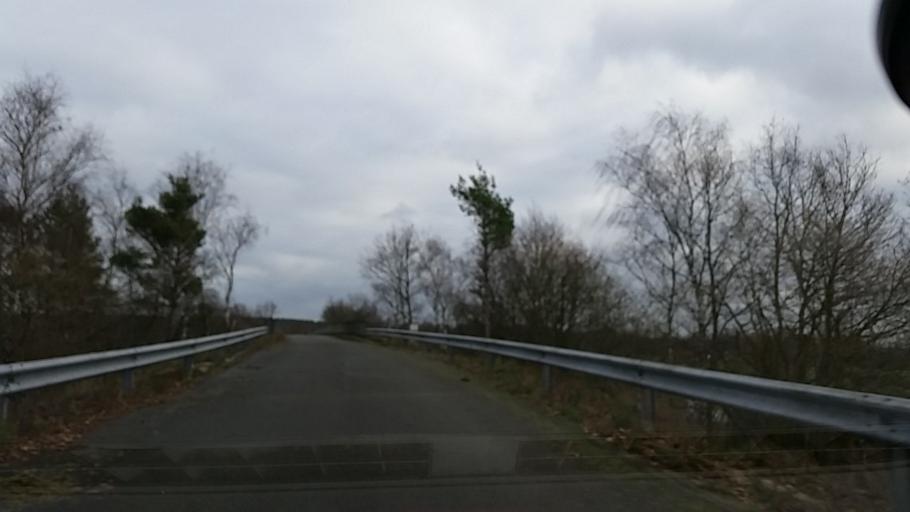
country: DE
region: Lower Saxony
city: Wieren
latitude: 52.8635
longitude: 10.6599
